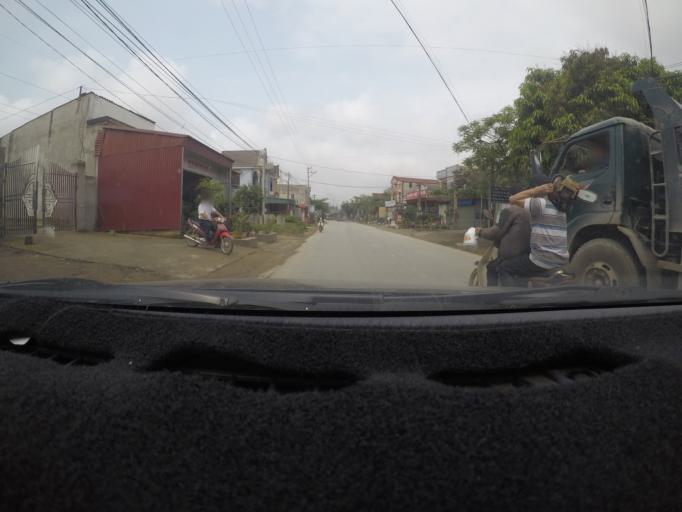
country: VN
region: Phu Tho
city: Doan Hung
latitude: 21.6313
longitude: 105.1355
